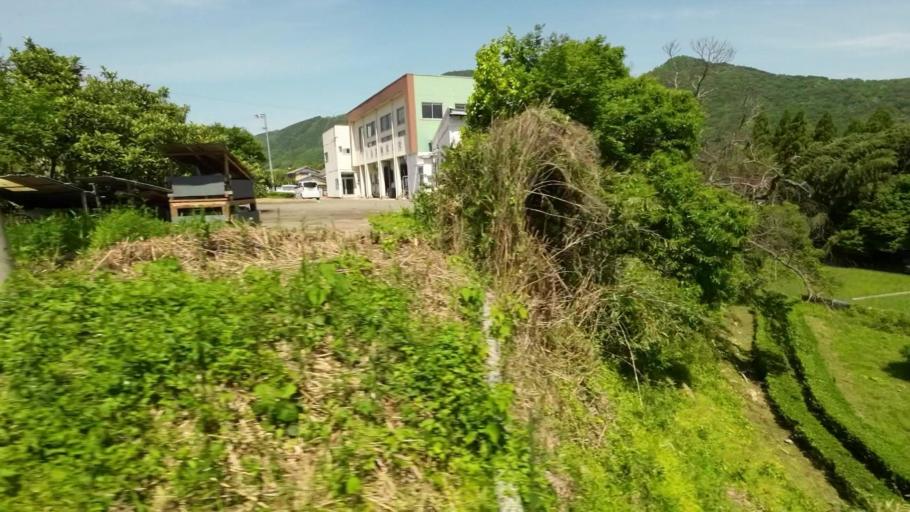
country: JP
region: Tokushima
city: Ikedacho
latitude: 34.0340
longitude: 133.8627
